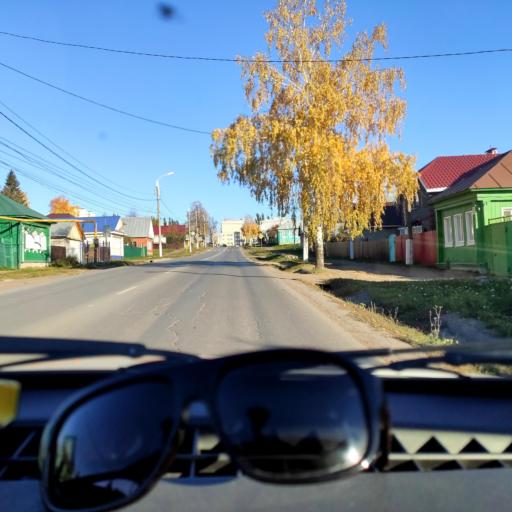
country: RU
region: Bashkortostan
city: Blagoveshchensk
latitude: 55.0430
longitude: 55.9606
